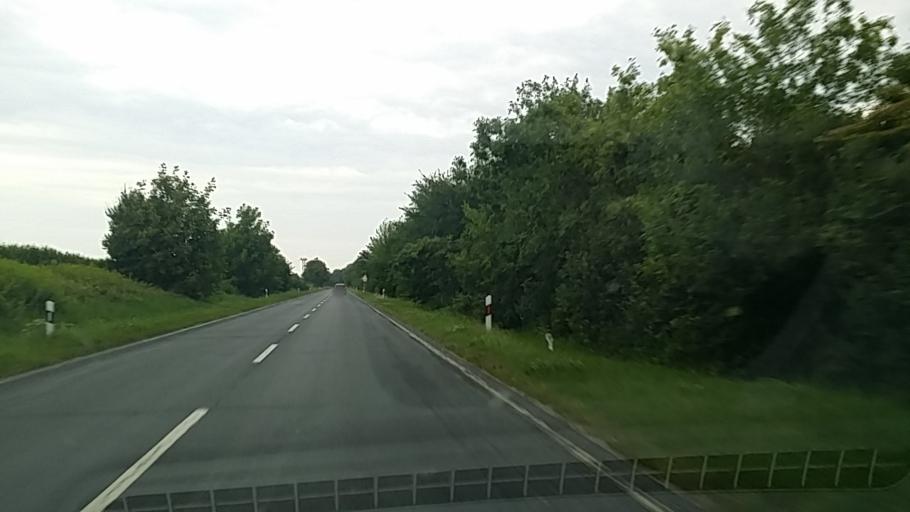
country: HU
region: Zala
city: Zalakomar
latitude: 46.5266
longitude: 17.1550
